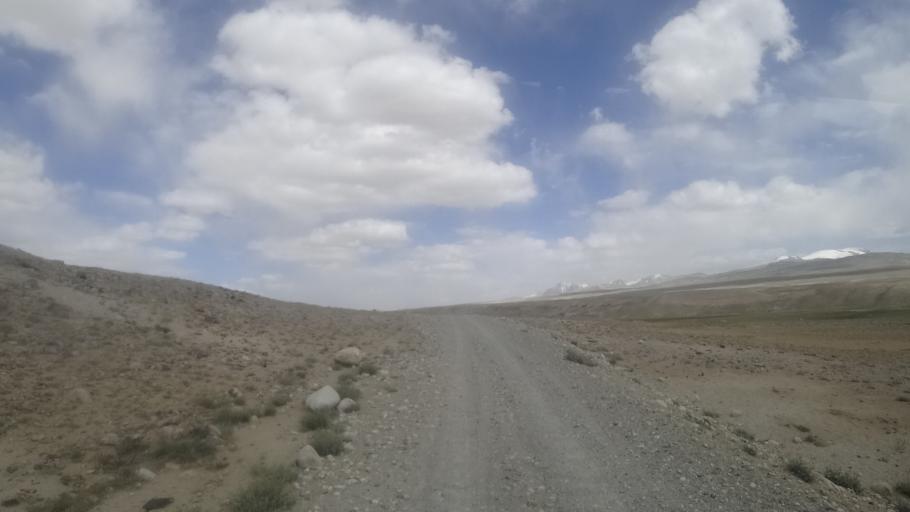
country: AF
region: Badakhshan
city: Khandud
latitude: 37.4063
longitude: 73.2047
